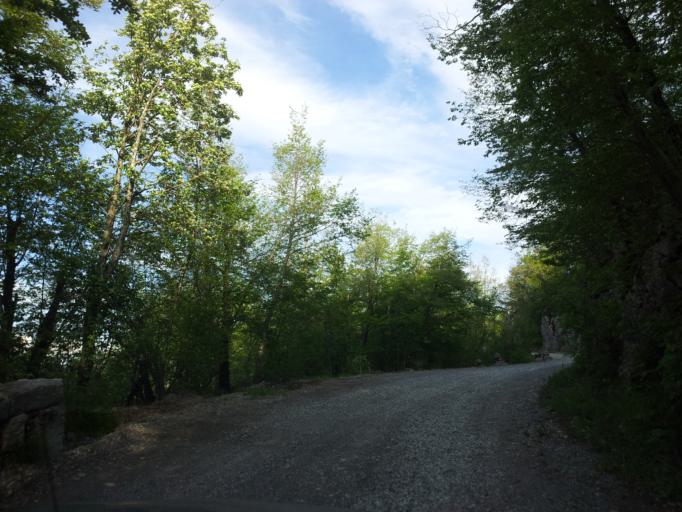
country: HR
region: Zadarska
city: Obrovac
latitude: 44.3028
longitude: 15.6612
